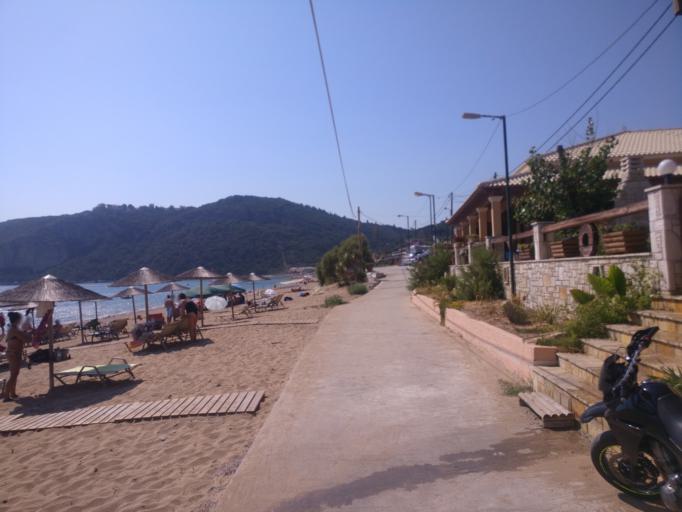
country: GR
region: Ionian Islands
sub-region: Nomos Kerkyras
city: Agios Georgis
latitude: 39.7205
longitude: 19.6735
